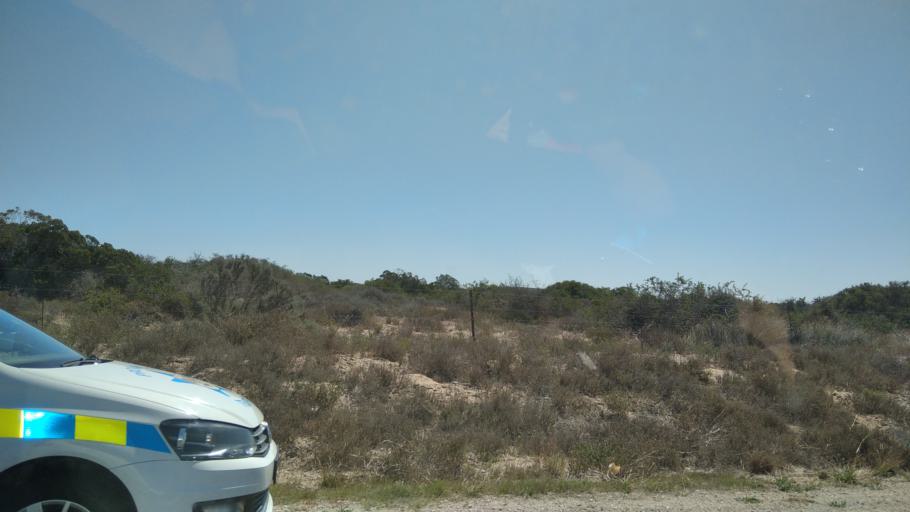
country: ZA
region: Western Cape
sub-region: West Coast District Municipality
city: Vredenburg
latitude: -32.9950
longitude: 18.1312
